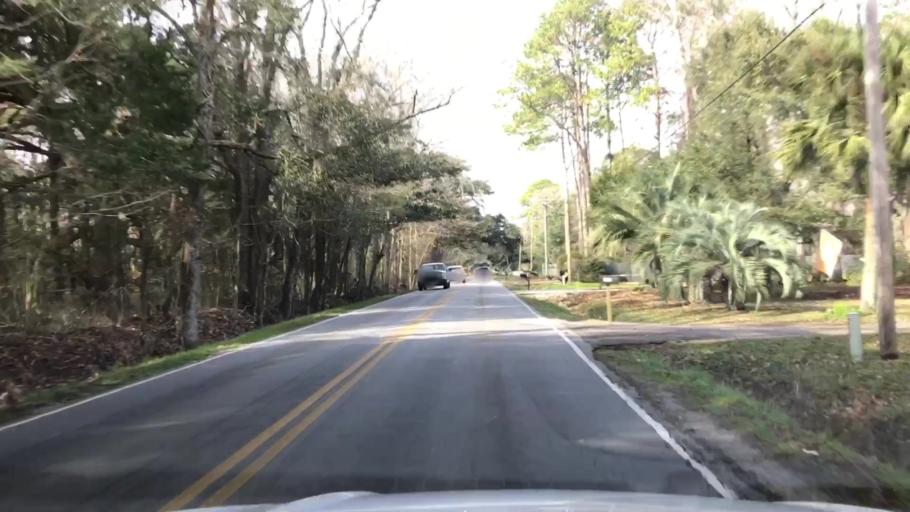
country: US
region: South Carolina
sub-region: Charleston County
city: Shell Point
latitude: 32.7648
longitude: -80.0637
